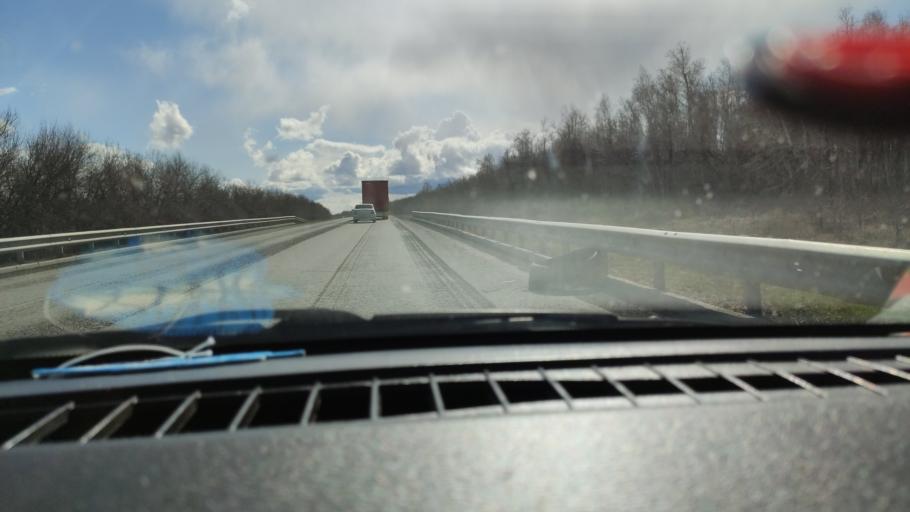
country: RU
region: Saratov
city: Dukhovnitskoye
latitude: 52.6492
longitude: 48.1983
